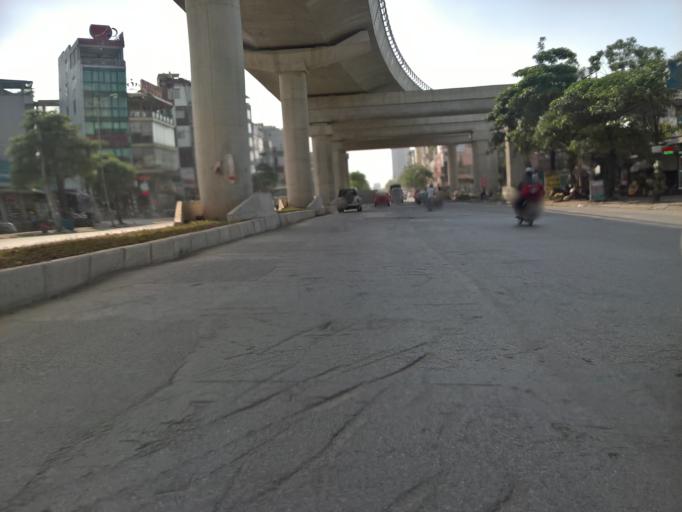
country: VN
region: Ha Noi
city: Troi
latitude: 21.0536
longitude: 105.7339
